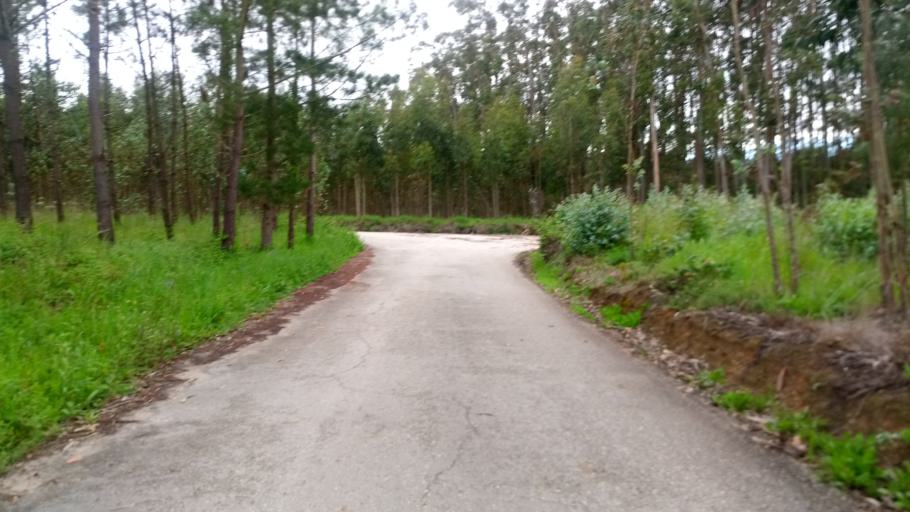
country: PT
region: Leiria
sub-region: Caldas da Rainha
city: Caldas da Rainha
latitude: 39.4570
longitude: -9.1773
